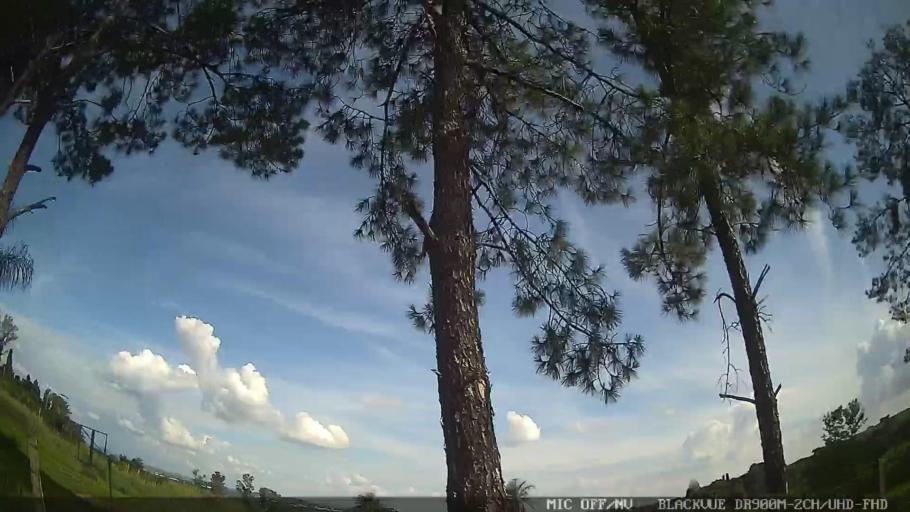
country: BR
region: Sao Paulo
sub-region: Jaguariuna
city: Jaguariuna
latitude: -22.6558
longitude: -47.0399
